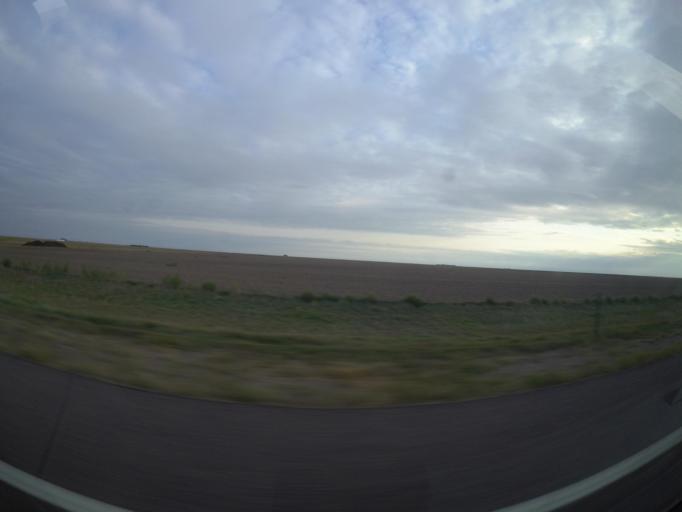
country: US
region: Colorado
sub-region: Yuma County
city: Wray
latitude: 39.7460
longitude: -102.1831
